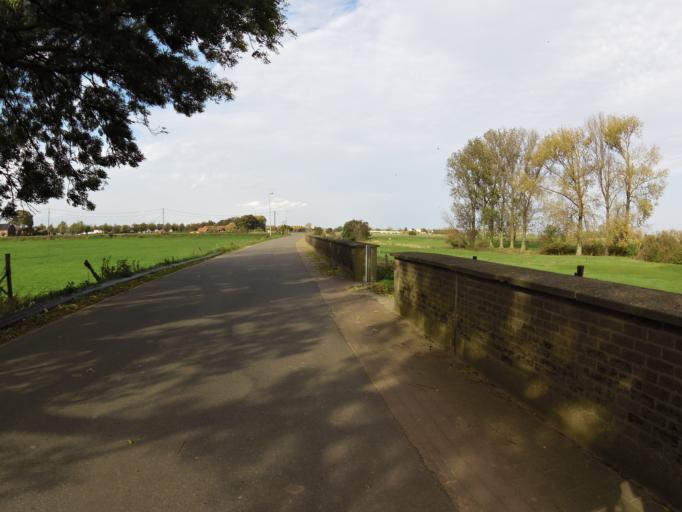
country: BE
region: Flanders
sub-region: Provincie Limburg
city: Maaseik
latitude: 51.0822
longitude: 5.7947
